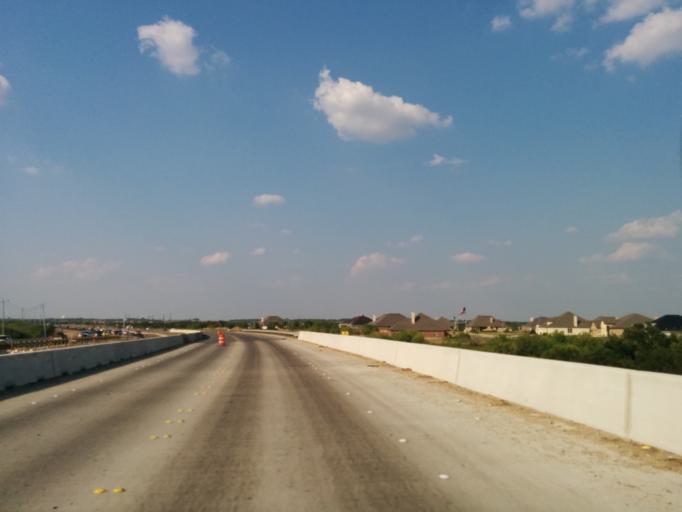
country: US
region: Texas
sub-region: Bexar County
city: Converse
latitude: 29.4852
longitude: -98.2930
